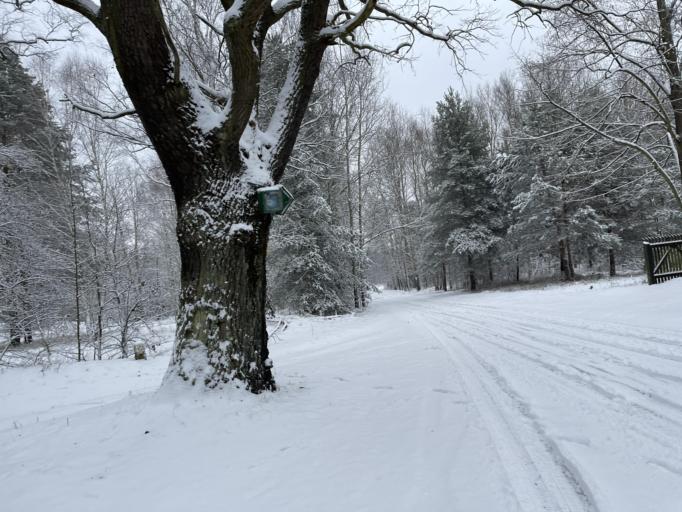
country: PL
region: Masovian Voivodeship
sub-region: Powiat zyrardowski
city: Guzow
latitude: 52.0487
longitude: 20.2736
